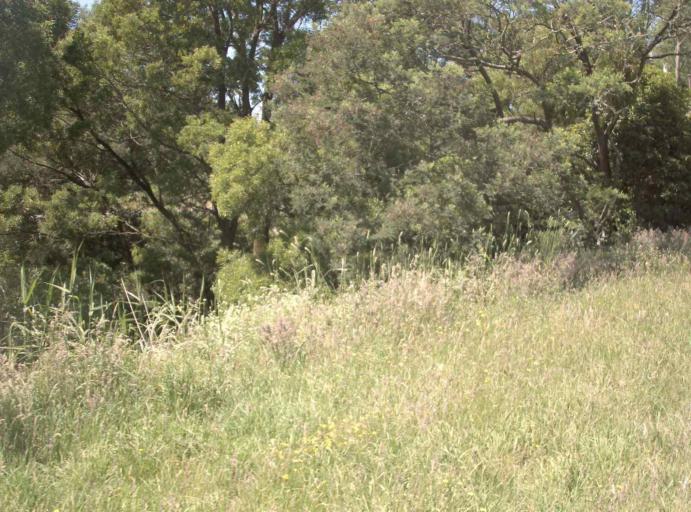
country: AU
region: Victoria
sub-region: Bass Coast
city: North Wonthaggi
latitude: -38.6935
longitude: 146.1167
